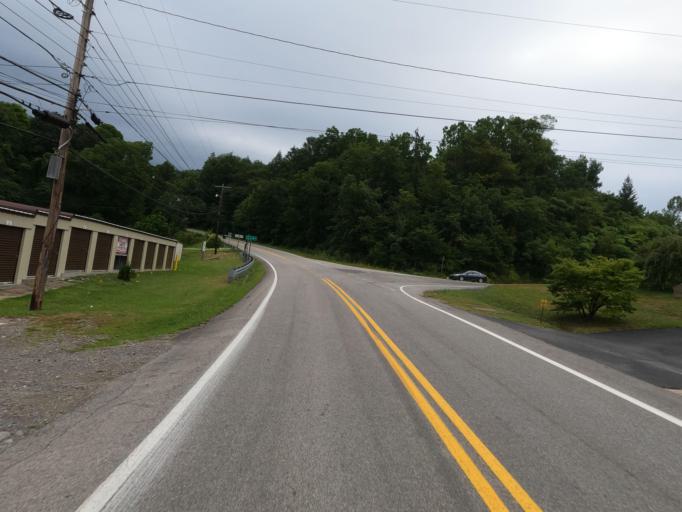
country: US
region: West Virginia
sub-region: Marion County
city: Fairmont
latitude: 39.4955
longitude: -80.0921
